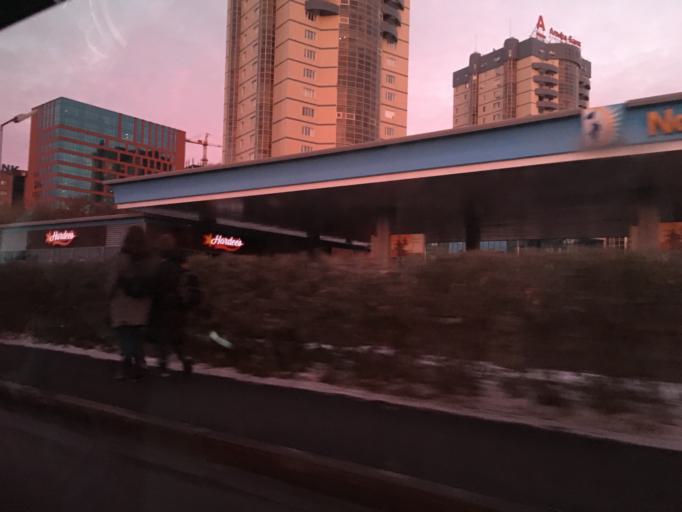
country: KZ
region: Astana Qalasy
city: Astana
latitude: 51.1458
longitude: 71.4219
